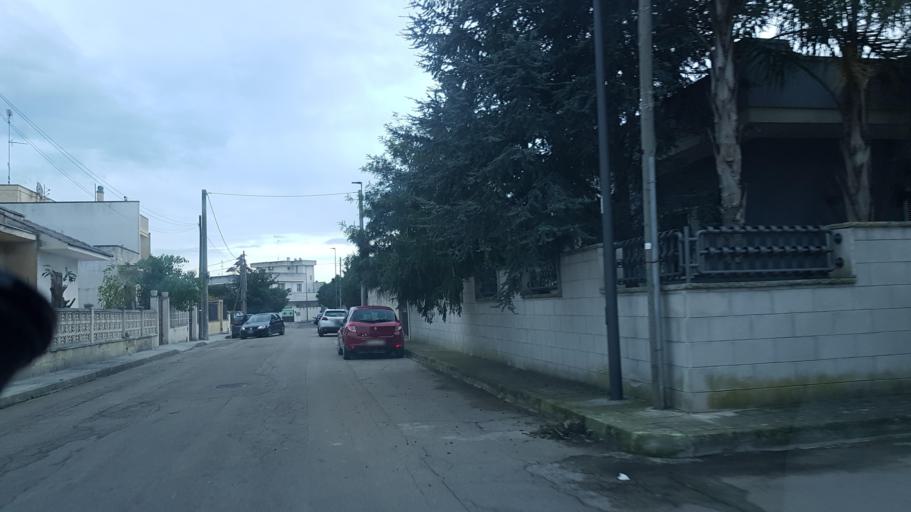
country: IT
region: Apulia
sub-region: Provincia di Lecce
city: Merine
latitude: 40.3309
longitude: 18.2212
